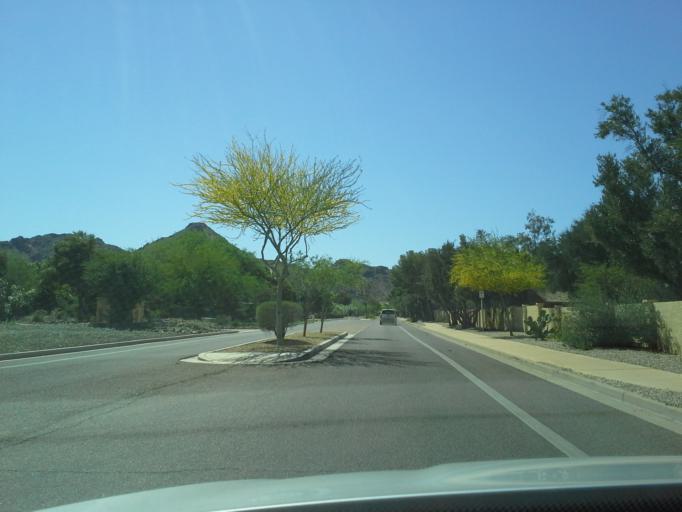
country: US
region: Arizona
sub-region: Maricopa County
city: Paradise Valley
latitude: 33.5531
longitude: -111.9378
